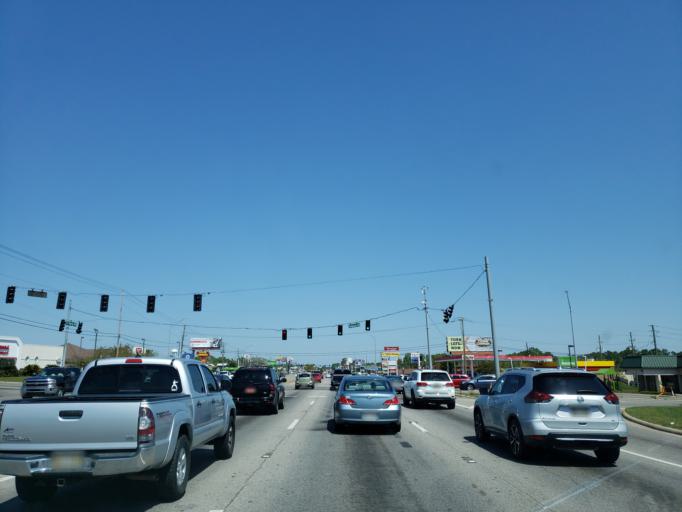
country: US
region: Mississippi
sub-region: Harrison County
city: West Gulfport
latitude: 30.4490
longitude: -89.0992
